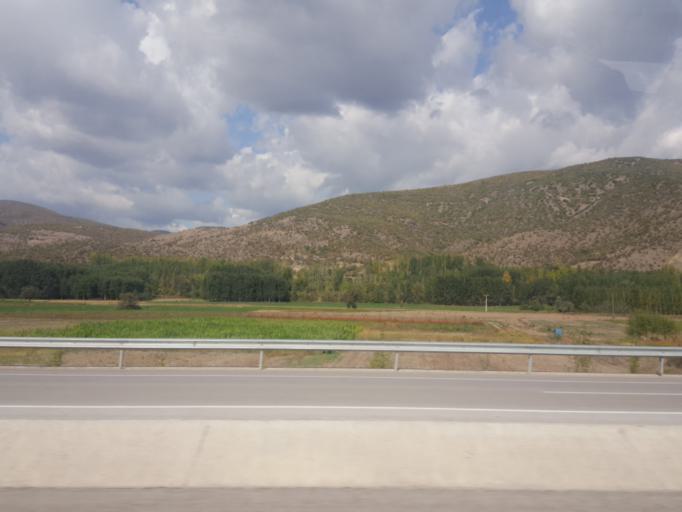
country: TR
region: Tokat
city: Gokdere
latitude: 40.3840
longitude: 36.6952
